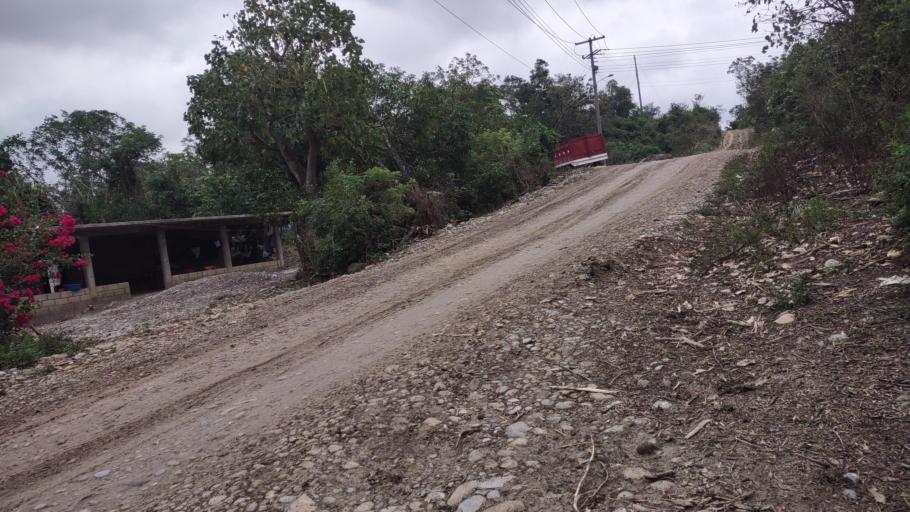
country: MX
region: Veracruz
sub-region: Coatzintla
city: Manuel Maria Contreras
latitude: 20.4114
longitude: -97.4583
